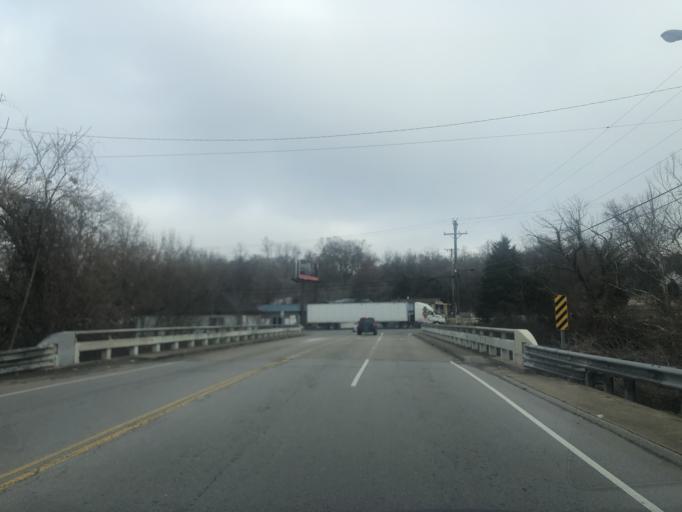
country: US
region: Tennessee
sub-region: Rutherford County
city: La Vergne
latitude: 36.0592
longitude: -86.6724
